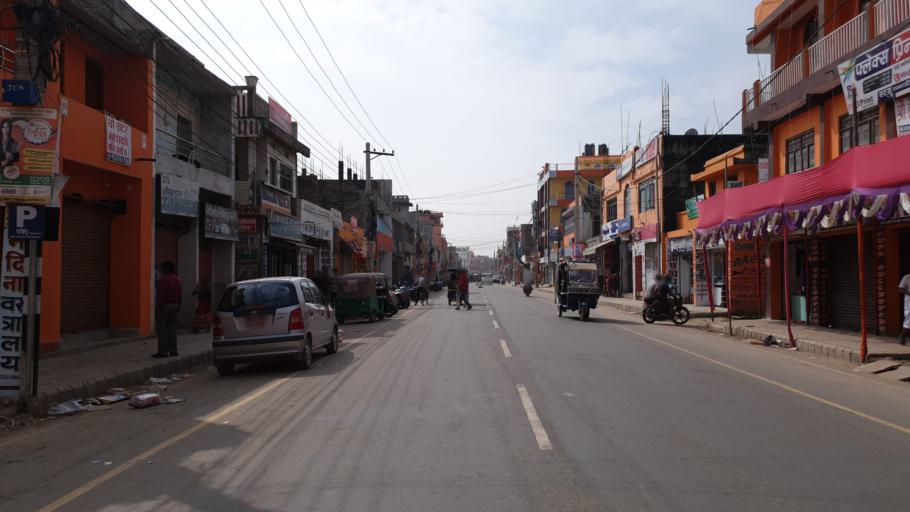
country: NP
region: Central Region
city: Janakpur
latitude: 26.7313
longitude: 85.9322
